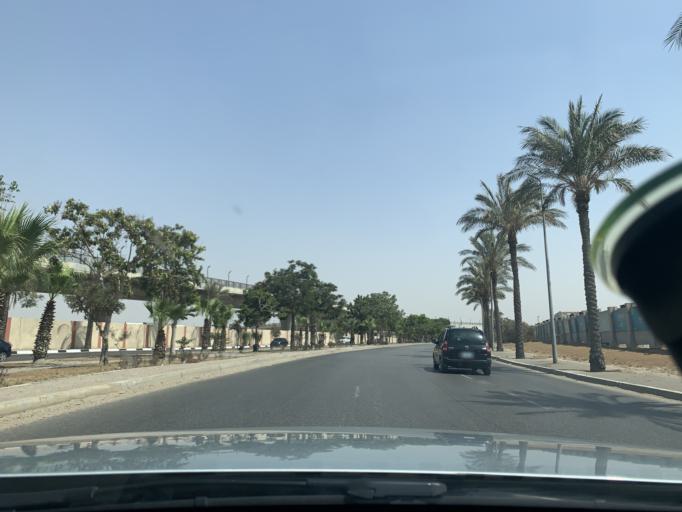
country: EG
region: Muhafazat al Qalyubiyah
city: Al Khankah
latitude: 30.1120
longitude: 31.3823
